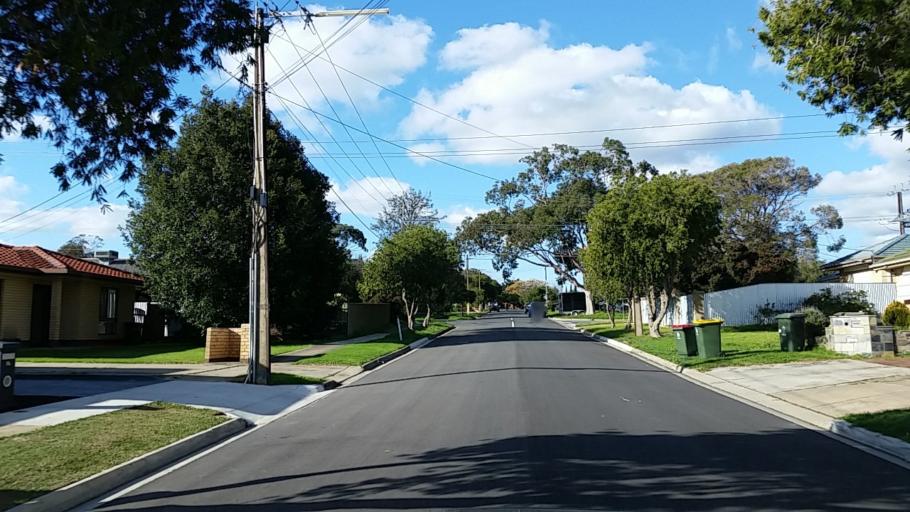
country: AU
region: South Australia
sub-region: Tea Tree Gully
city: Modbury
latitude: -34.8512
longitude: 138.6743
